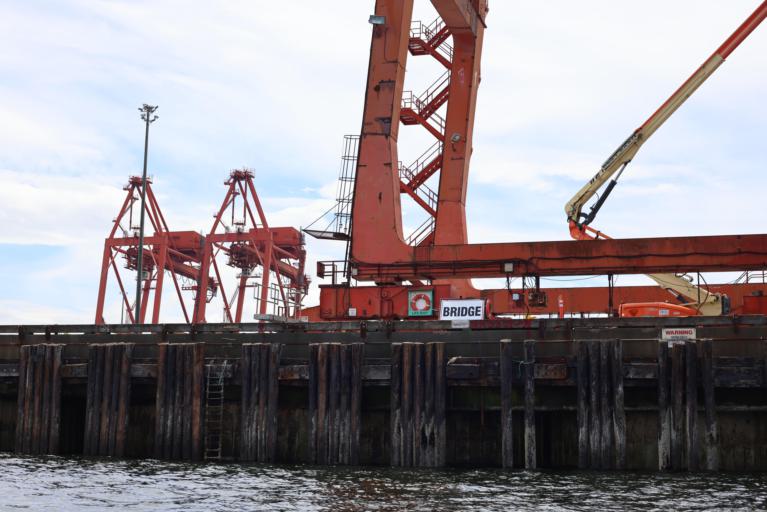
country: CA
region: British Columbia
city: Nanaimo
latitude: 49.1501
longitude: -123.8792
